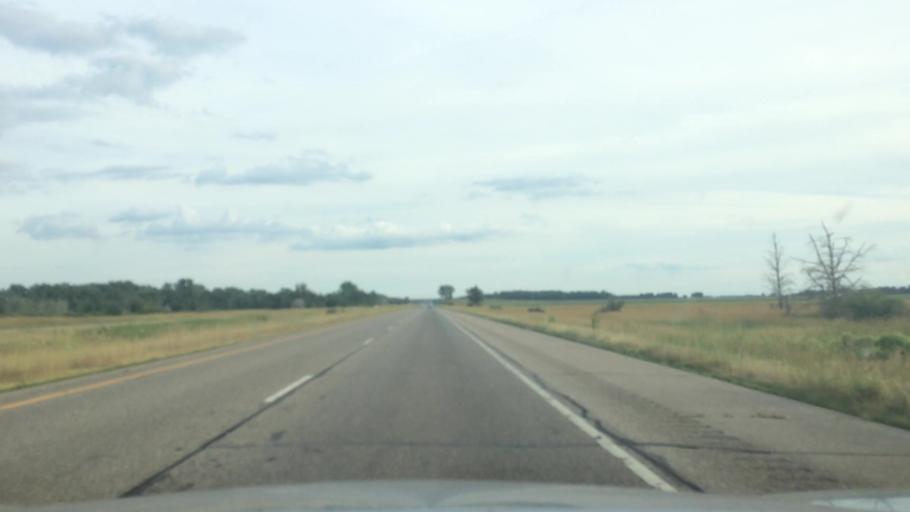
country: US
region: Wisconsin
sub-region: Waushara County
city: Wautoma
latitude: 44.1647
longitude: -89.5327
